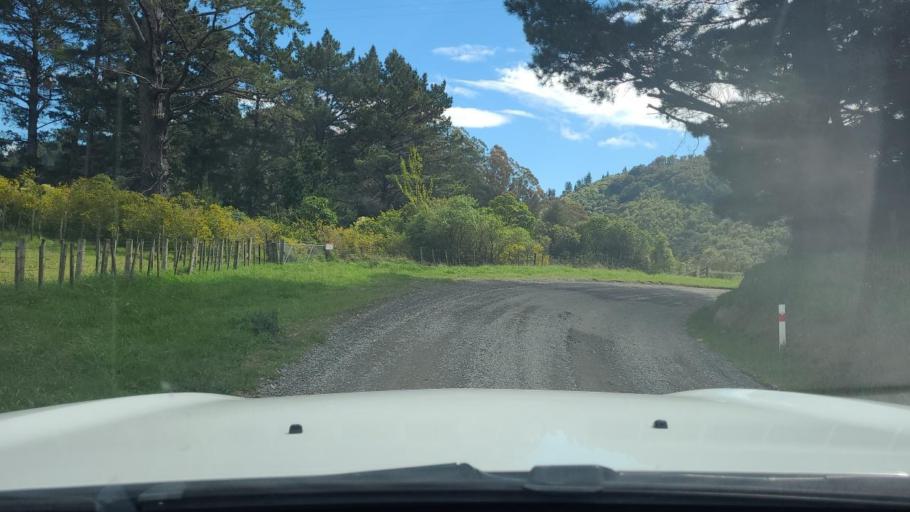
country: NZ
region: Wellington
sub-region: South Wairarapa District
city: Waipawa
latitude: -41.3201
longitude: 175.3767
